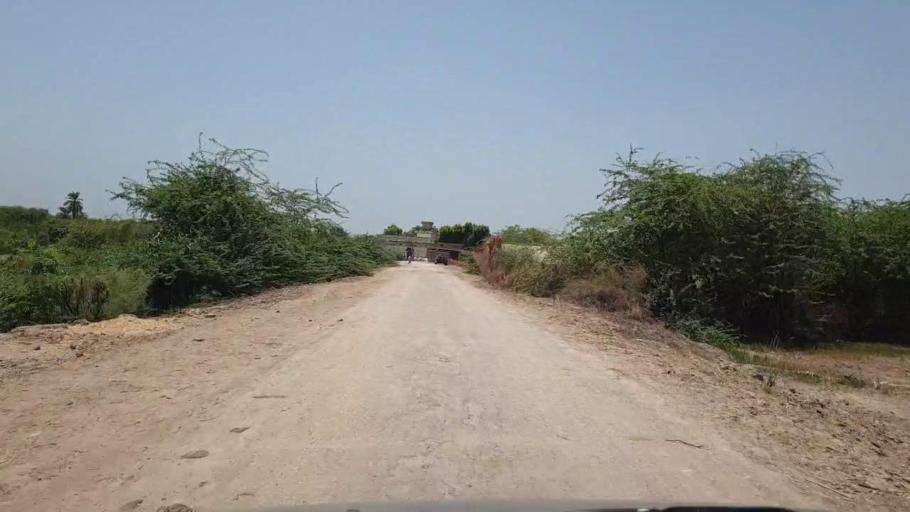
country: PK
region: Sindh
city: Sakrand
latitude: 26.1094
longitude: 68.3898
